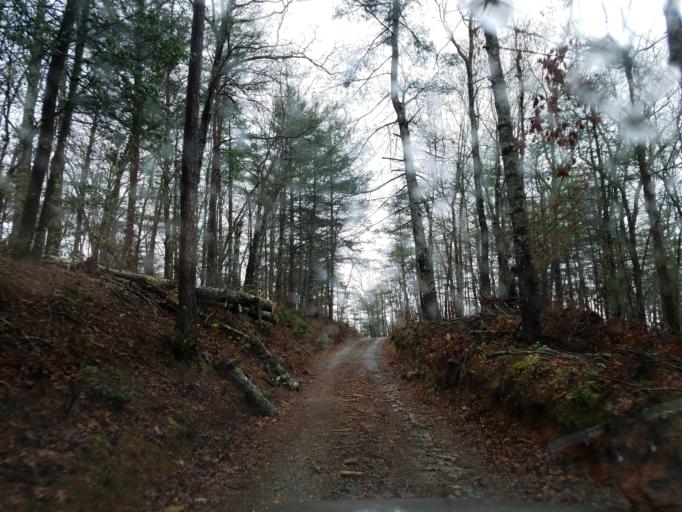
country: US
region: Georgia
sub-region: Fannin County
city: Blue Ridge
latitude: 34.8312
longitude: -84.2378
